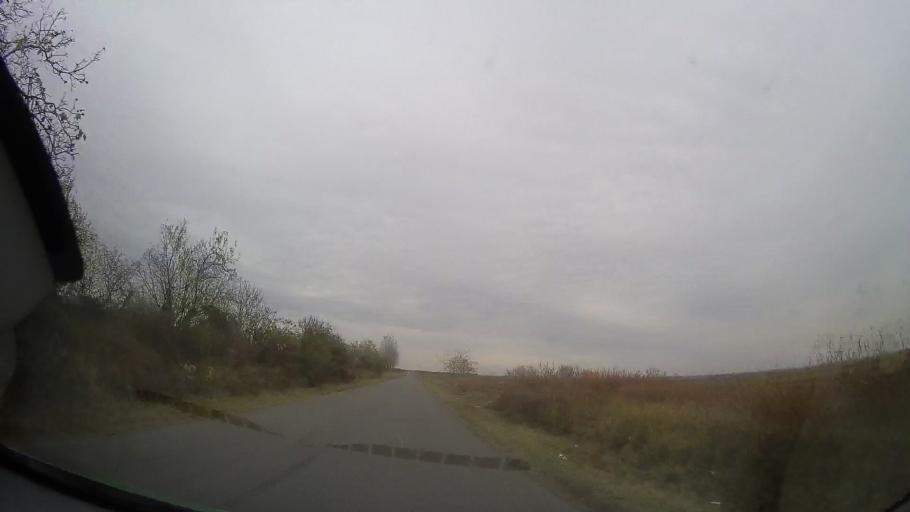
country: RO
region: Prahova
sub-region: Comuna Ceptura
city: Ceptura de Jos
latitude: 45.0139
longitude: 26.3443
